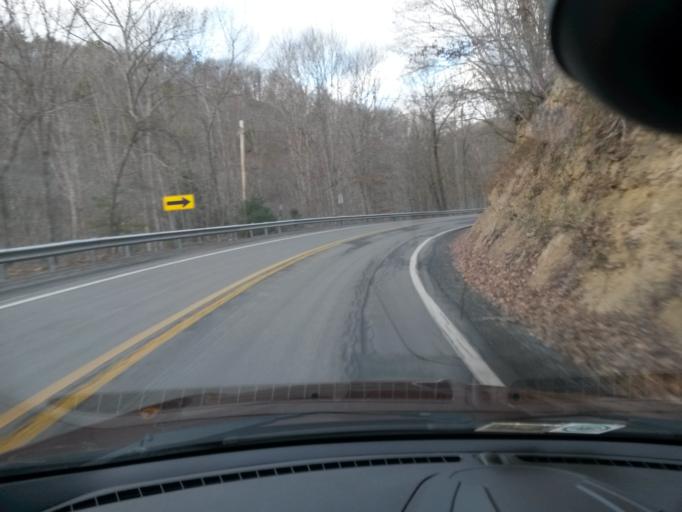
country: US
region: West Virginia
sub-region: Monroe County
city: Union
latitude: 37.5050
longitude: -80.6116
